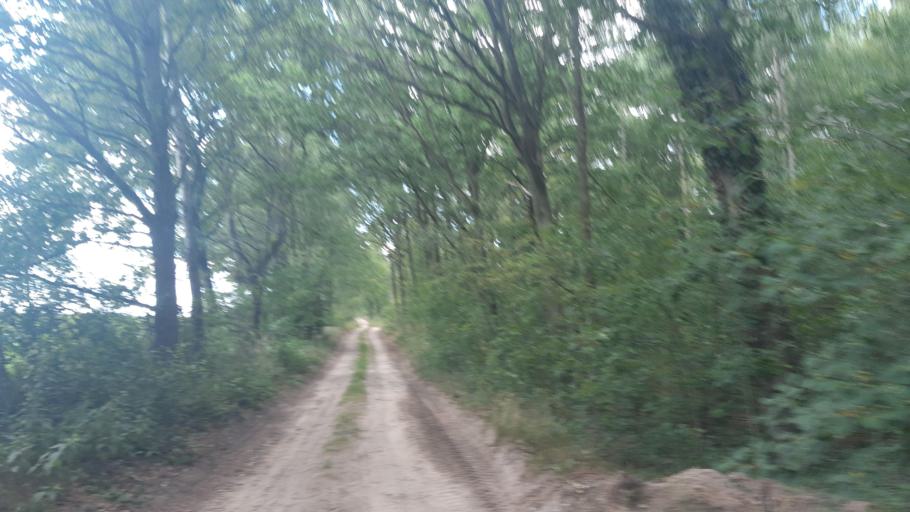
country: DE
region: Lower Saxony
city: Dahlem
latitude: 53.2059
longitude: 10.7780
